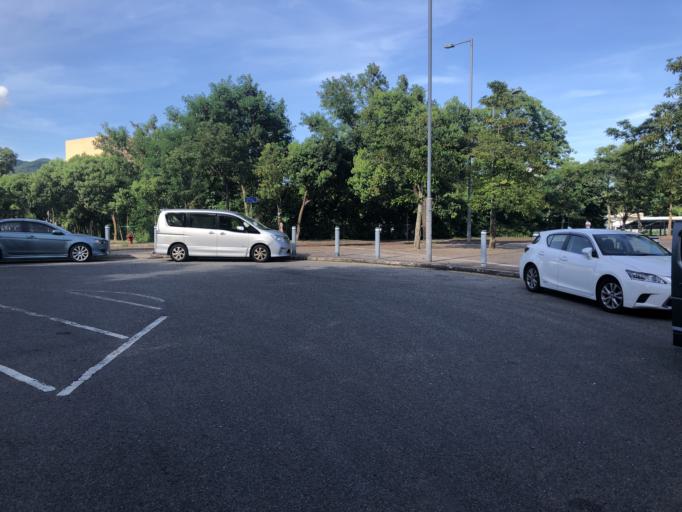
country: HK
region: Sai Kung
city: Sai Kung
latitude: 22.3842
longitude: 114.2729
